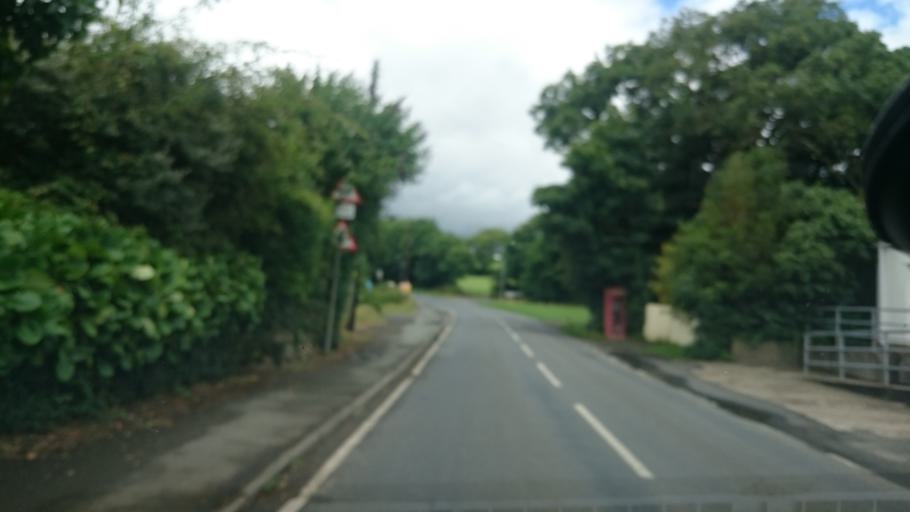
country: GB
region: Wales
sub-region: Pembrokeshire
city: Burton
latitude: 51.7272
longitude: -4.9210
